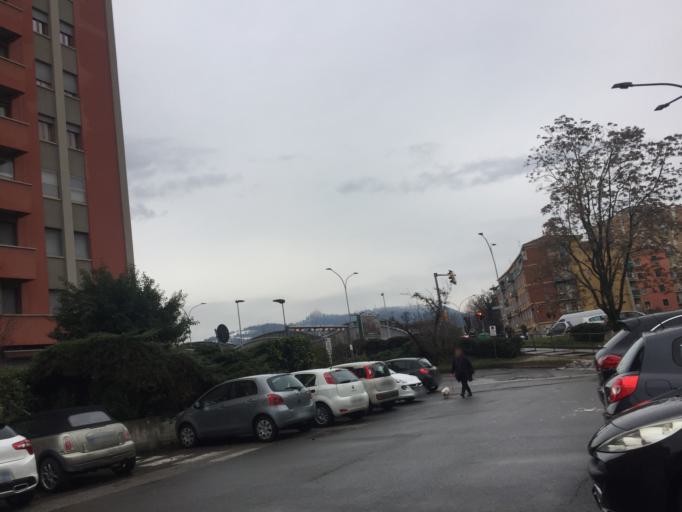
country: IT
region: Emilia-Romagna
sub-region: Provincia di Bologna
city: Casalecchio di Reno
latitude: 44.5043
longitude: 11.2949
